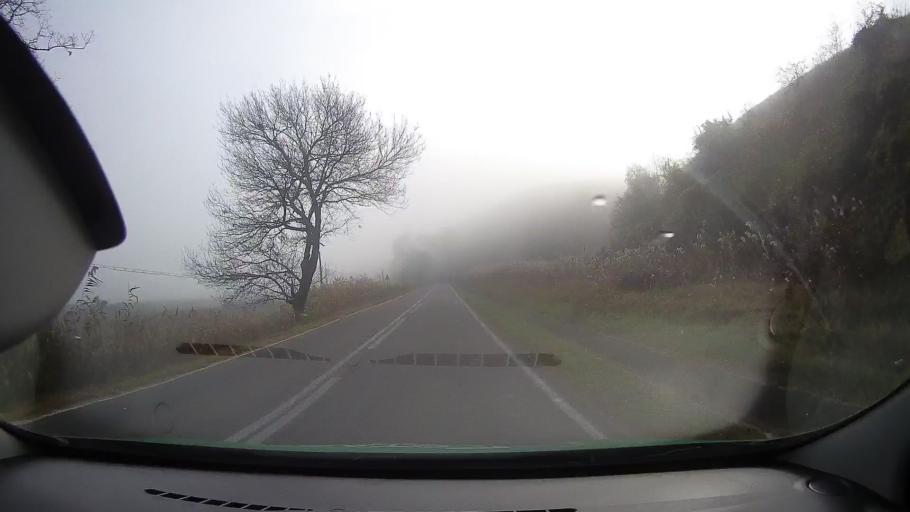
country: RO
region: Tulcea
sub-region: Comuna Nufaru
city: Malcoci
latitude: 45.1467
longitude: 28.8948
